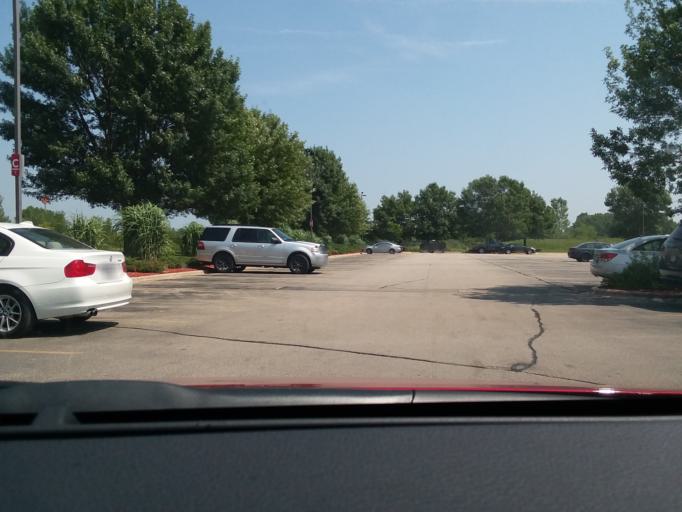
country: US
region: Wisconsin
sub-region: Dane County
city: McFarland
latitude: 43.0408
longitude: -89.2714
